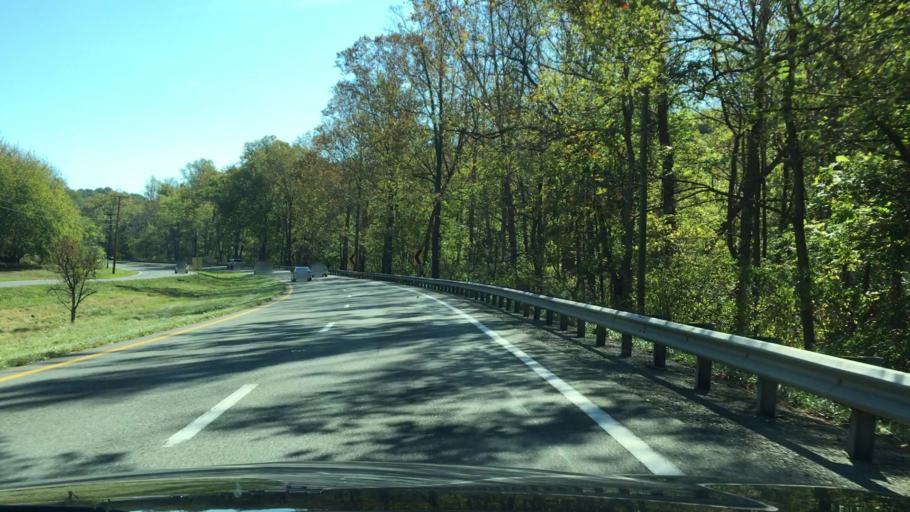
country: US
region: Virginia
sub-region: Roanoke County
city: Narrows
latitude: 37.1302
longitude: -79.9686
